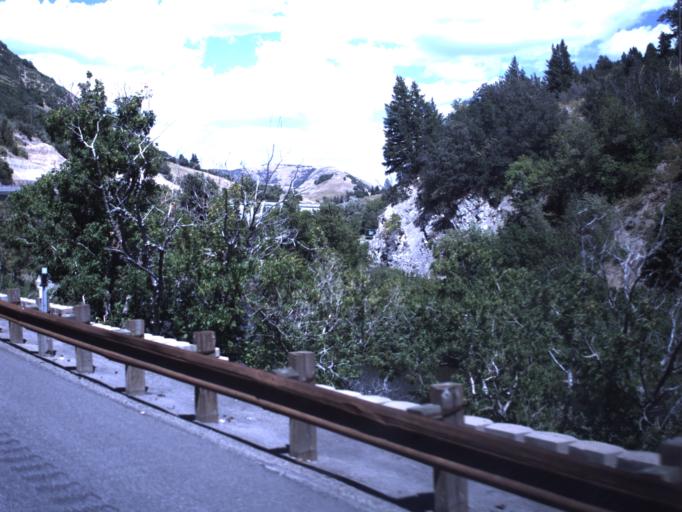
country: US
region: Utah
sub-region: Utah County
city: Orem
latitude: 40.3747
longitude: -111.5560
